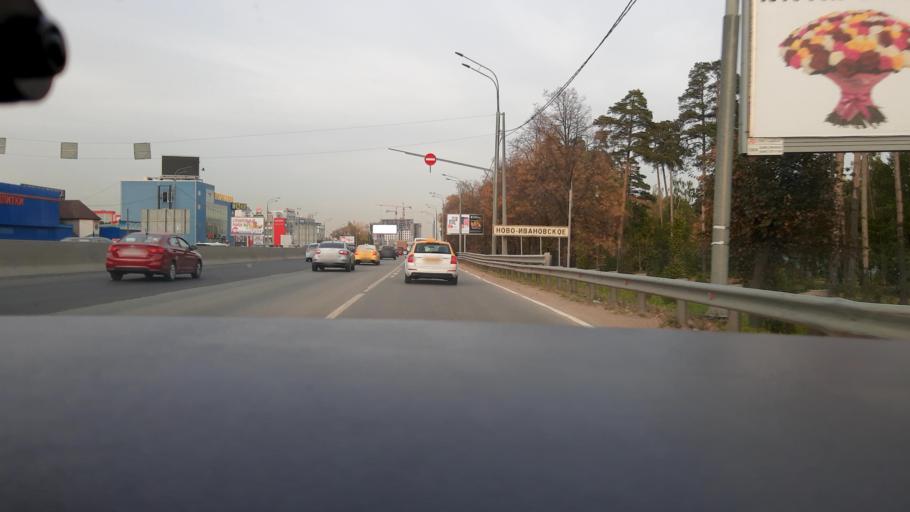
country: RU
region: Moskovskaya
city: Novoivanovskoye
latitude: 55.7057
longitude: 37.3585
